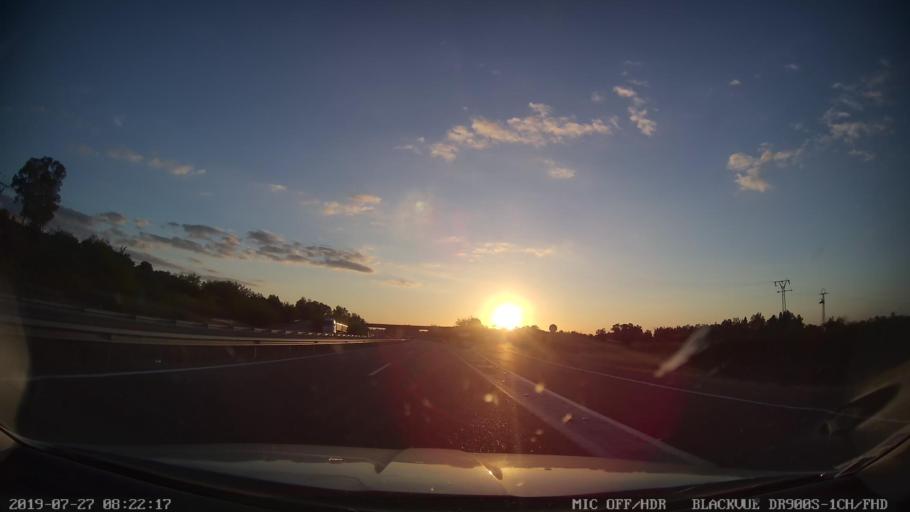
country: ES
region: Extremadura
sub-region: Provincia de Badajoz
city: Torremayor
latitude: 38.8611
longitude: -6.5428
